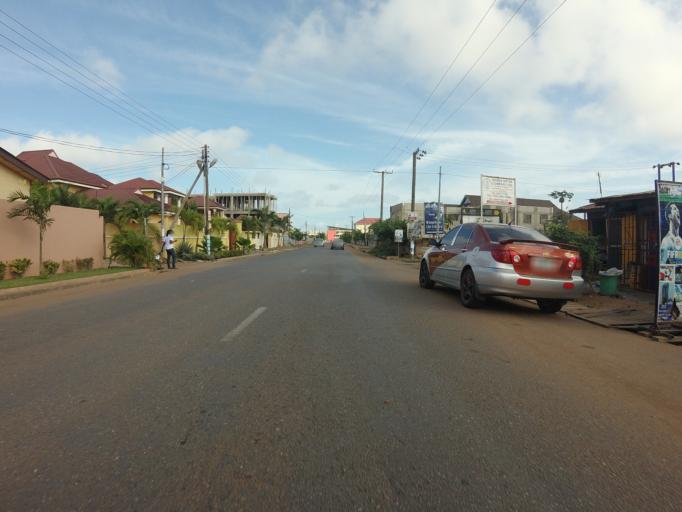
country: GH
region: Greater Accra
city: Teshi Old Town
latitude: 5.5781
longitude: -0.1400
